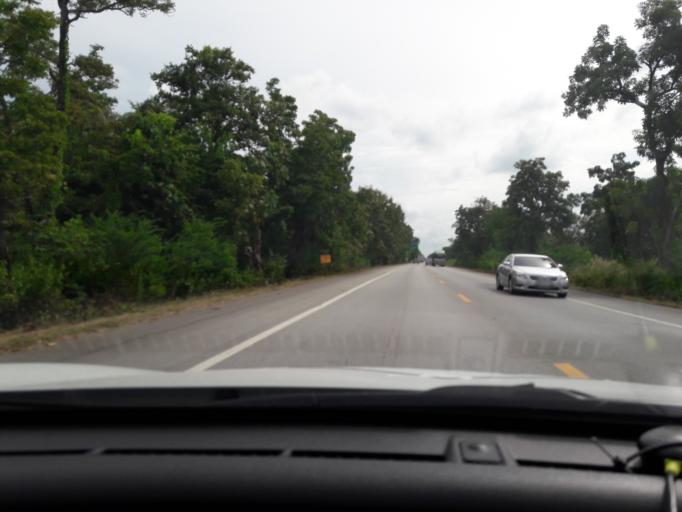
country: TH
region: Nakhon Sawan
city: Tak Fa
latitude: 15.4778
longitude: 100.5346
